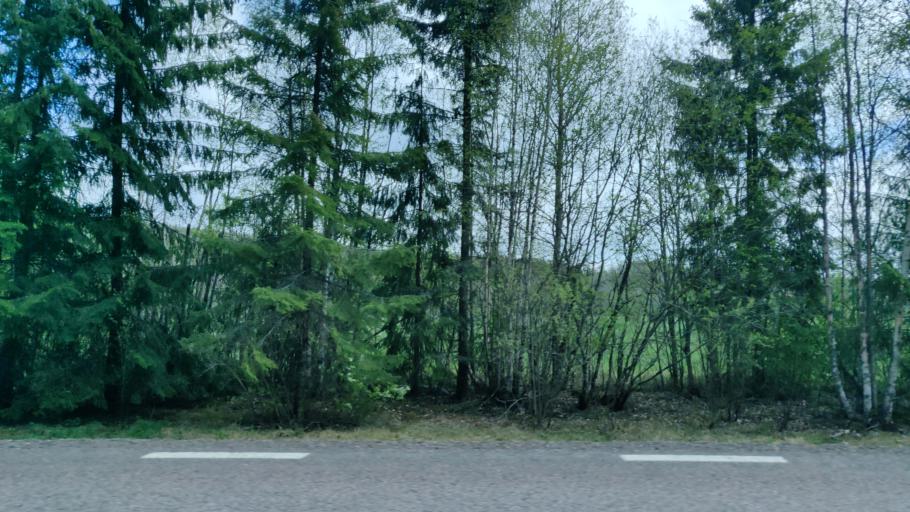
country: SE
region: Vaermland
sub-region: Karlstads Kommun
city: Molkom
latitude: 59.6251
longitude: 13.7303
